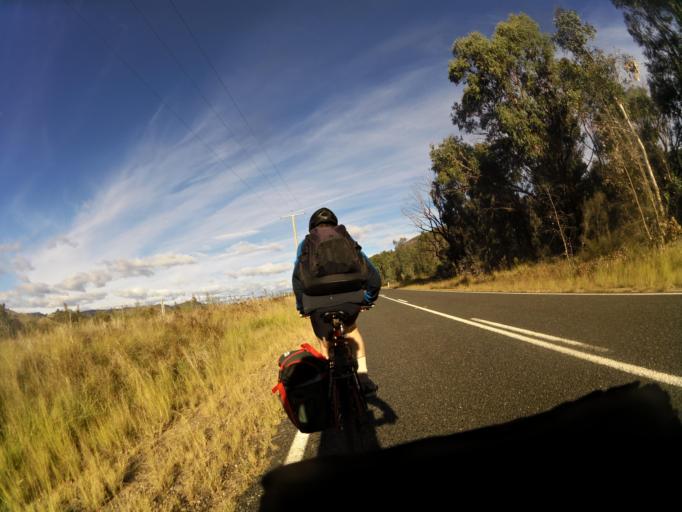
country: AU
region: New South Wales
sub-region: Greater Hume Shire
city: Holbrook
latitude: -35.9838
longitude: 147.8232
